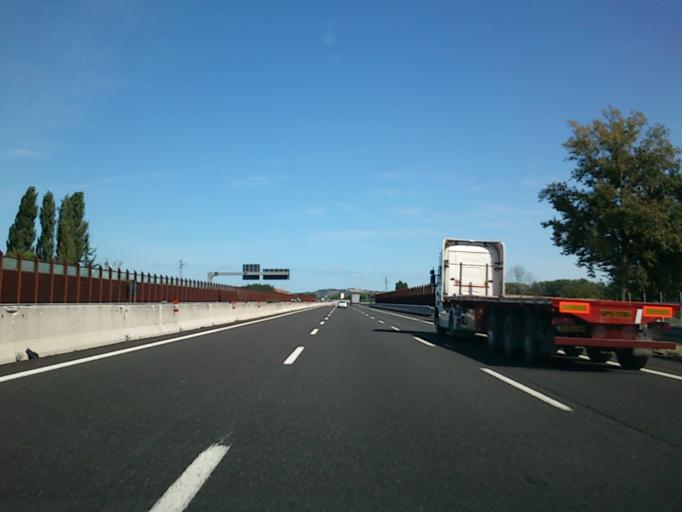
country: IT
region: The Marches
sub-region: Provincia di Pesaro e Urbino
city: Villa Ceccolini
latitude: 43.8992
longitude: 12.8531
